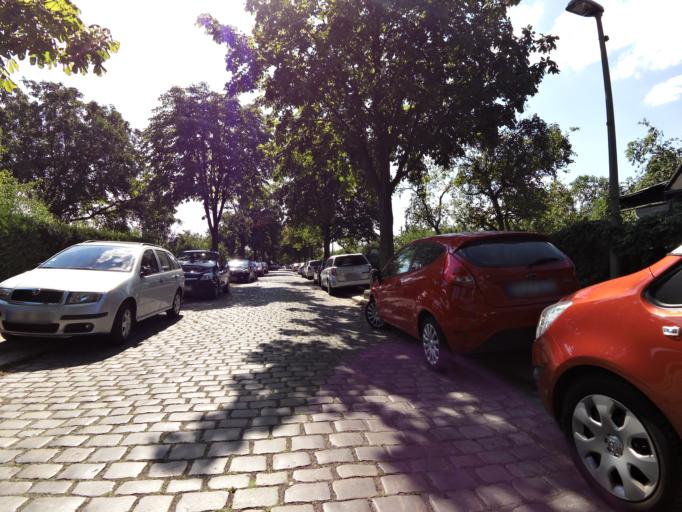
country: DE
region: Berlin
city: Schoneberg Bezirk
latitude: 52.4678
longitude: 13.3559
